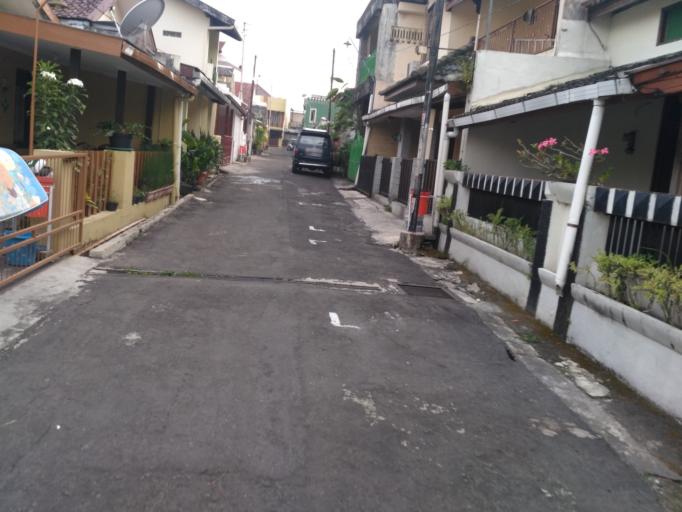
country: ID
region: Daerah Istimewa Yogyakarta
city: Melati
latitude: -7.7376
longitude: 110.3875
